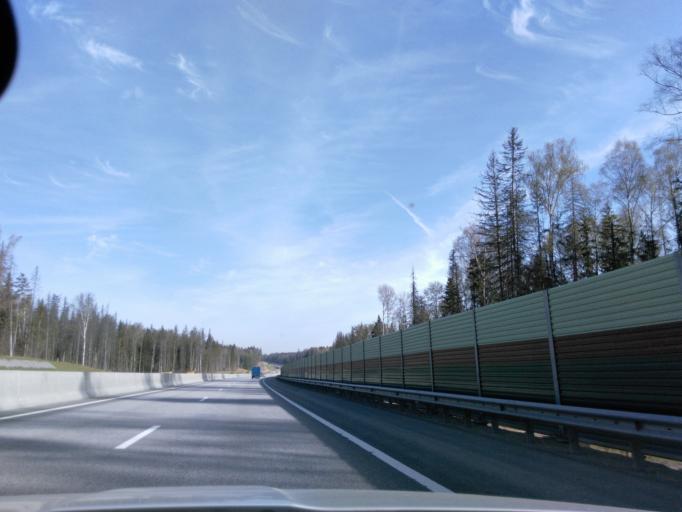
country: RU
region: Moskovskaya
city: Rzhavki
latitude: 56.0292
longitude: 37.2713
